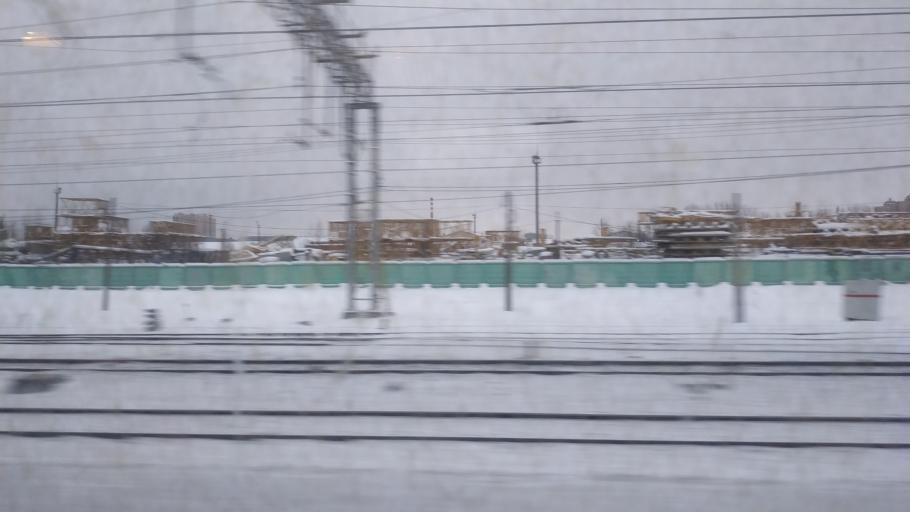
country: RU
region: Moskovskaya
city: Shcherbinka
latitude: 55.4764
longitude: 37.5548
